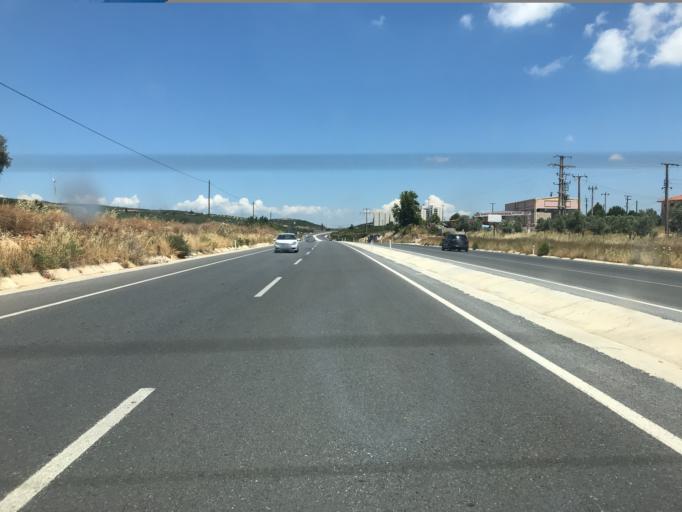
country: TR
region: Aydin
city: Akkoy
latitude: 37.4686
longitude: 27.3393
